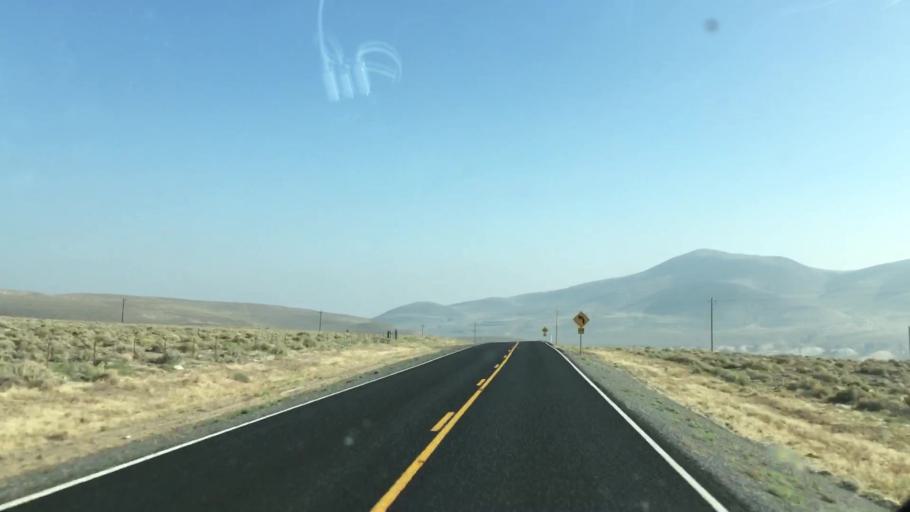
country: US
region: Nevada
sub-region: Lyon County
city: Fernley
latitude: 39.7316
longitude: -119.3327
